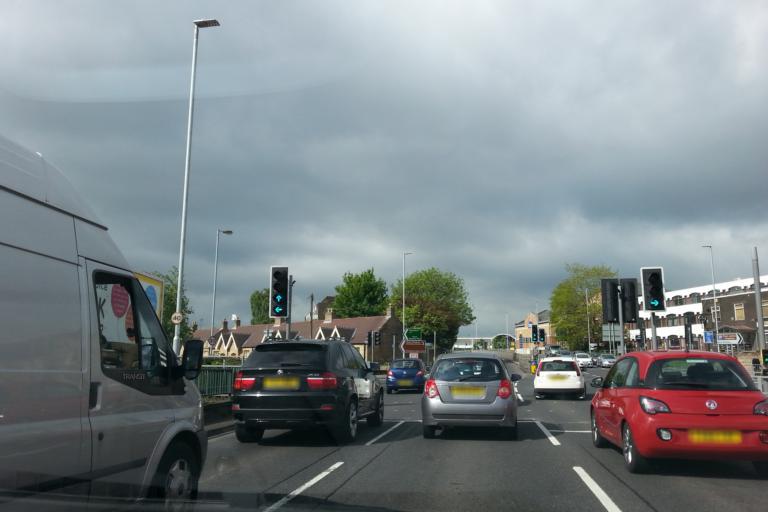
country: GB
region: England
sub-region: Nottinghamshire
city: Mansfield
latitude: 53.1420
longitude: -1.1947
